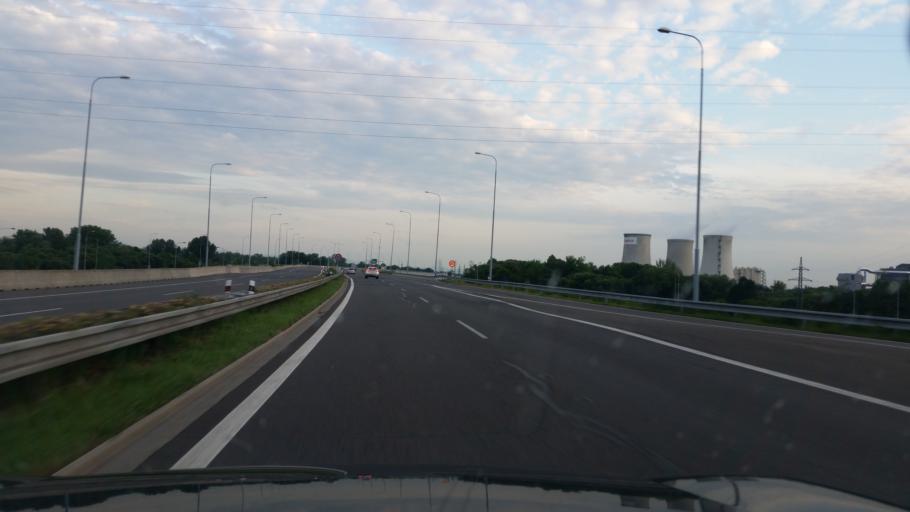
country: CZ
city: Ludgerovice
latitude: 49.8368
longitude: 18.2186
